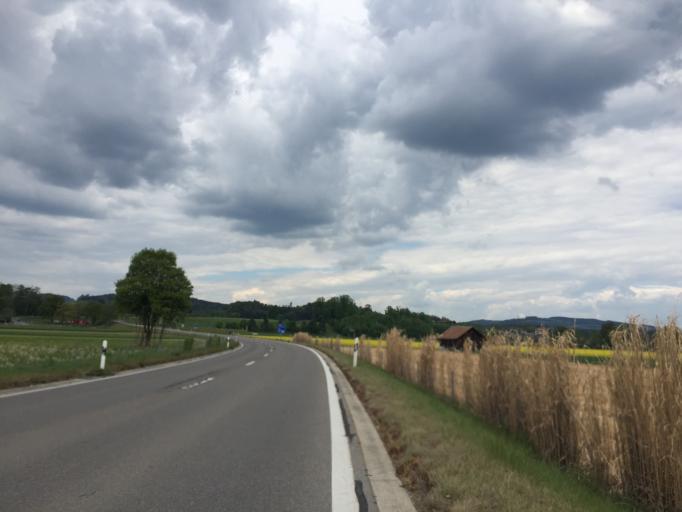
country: CH
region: Bern
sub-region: Thun District
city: Uttigen
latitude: 46.7849
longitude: 7.5802
